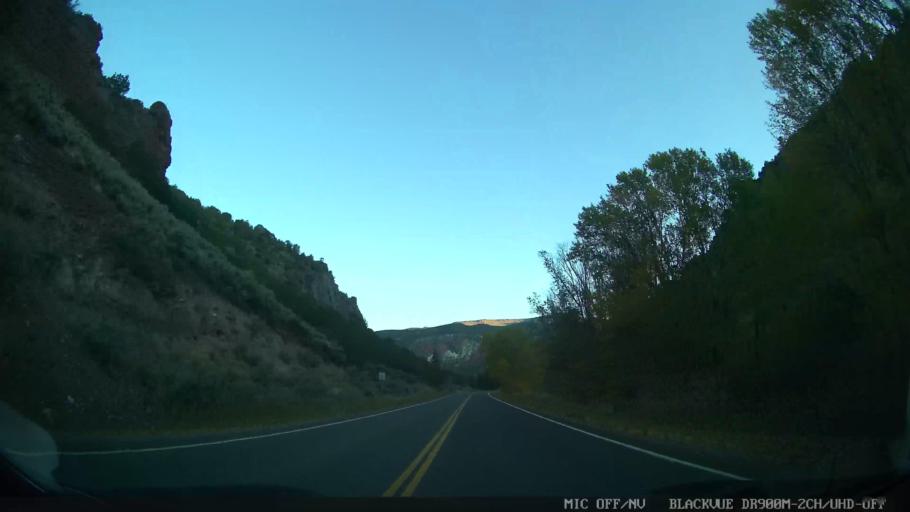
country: US
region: Colorado
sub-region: Eagle County
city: Edwards
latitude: 39.8480
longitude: -106.6432
